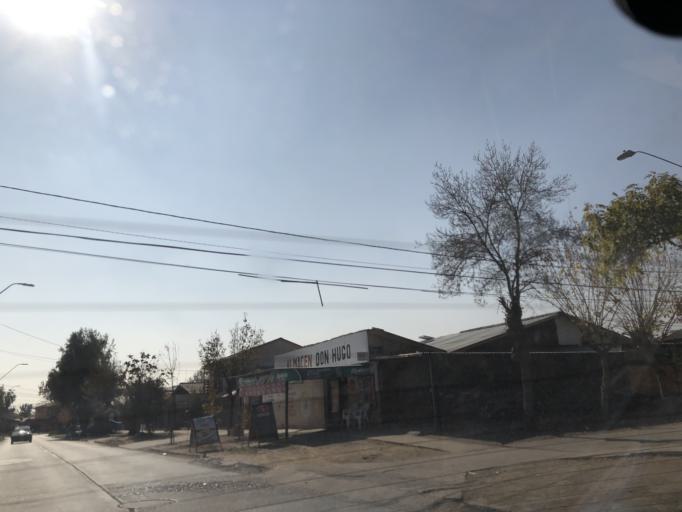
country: CL
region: Santiago Metropolitan
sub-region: Provincia de Cordillera
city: Puente Alto
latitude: -33.6214
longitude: -70.5880
